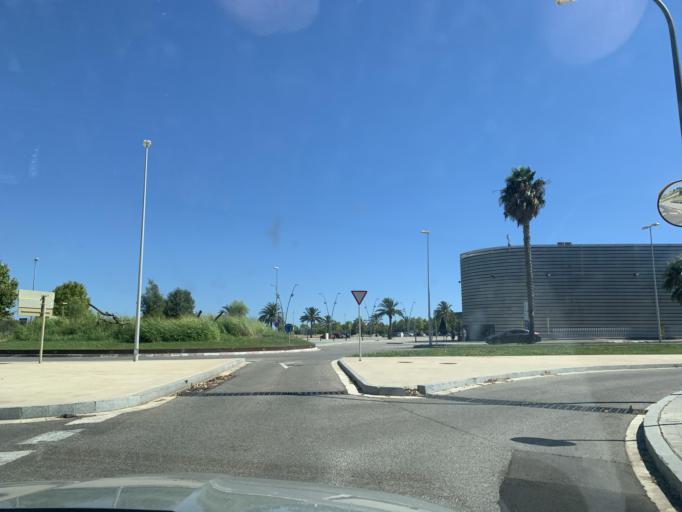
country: ES
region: Catalonia
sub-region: Provincia de Tarragona
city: Reus
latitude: 41.1444
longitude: 1.1292
